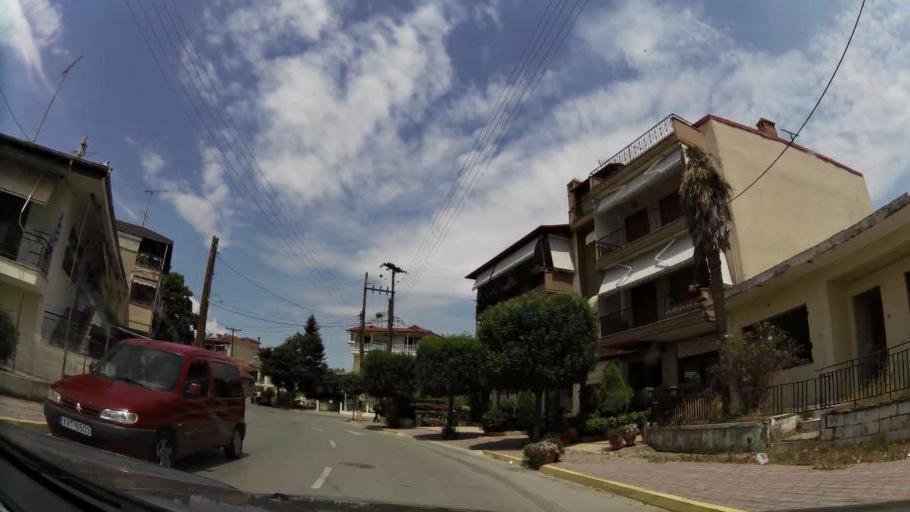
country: GR
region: Central Macedonia
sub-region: Nomos Pierias
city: Katerini
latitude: 40.2662
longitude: 22.5200
